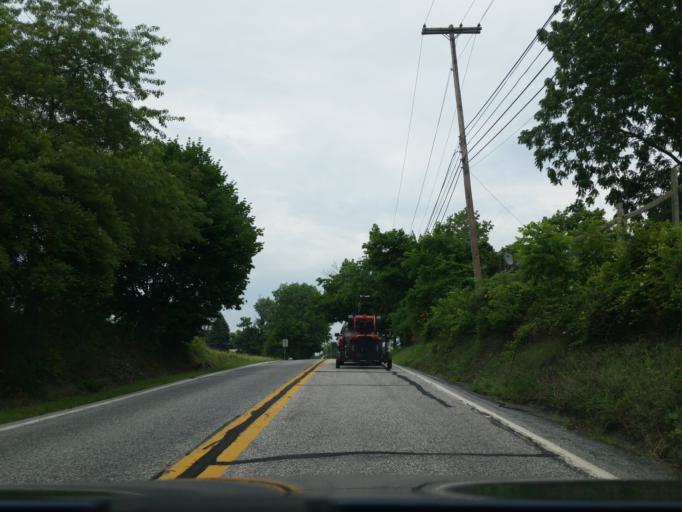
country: US
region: Pennsylvania
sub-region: Lebanon County
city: Palmyra
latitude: 40.3922
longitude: -76.6103
